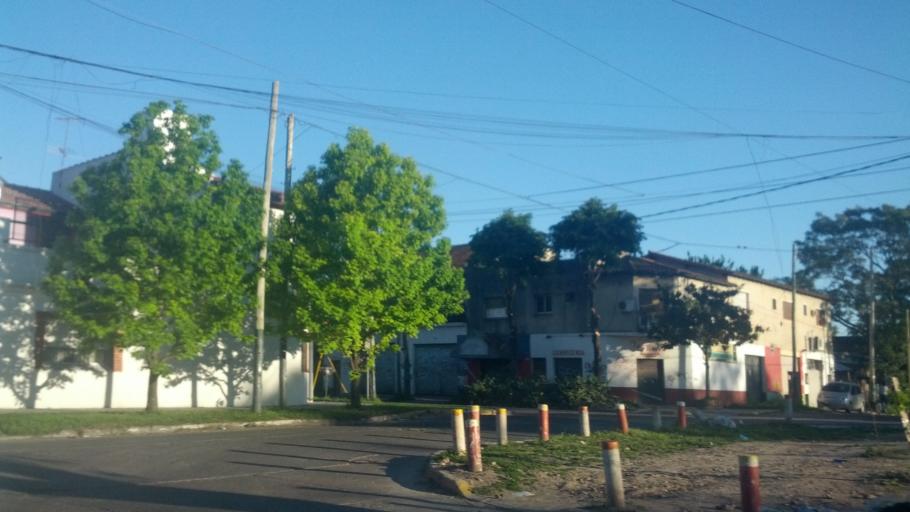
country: AR
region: Buenos Aires
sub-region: Partido de Lomas de Zamora
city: Lomas de Zamora
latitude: -34.7651
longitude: -58.4278
